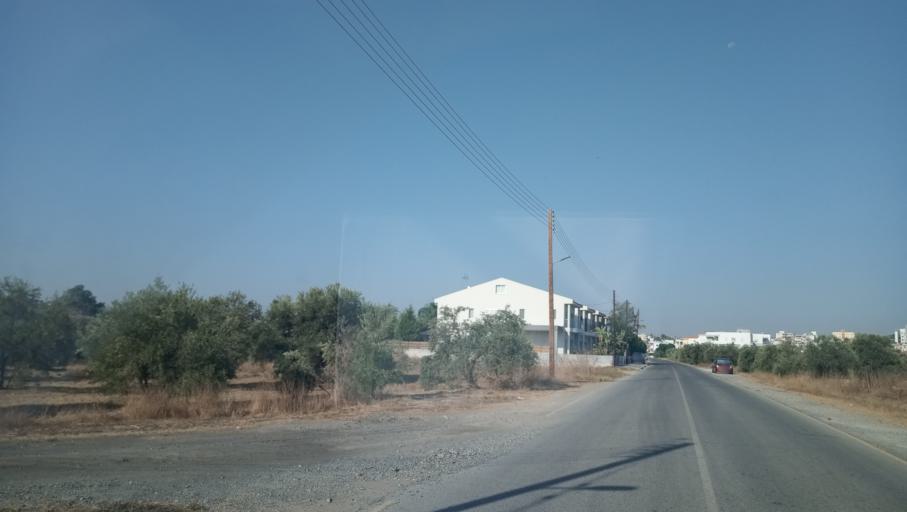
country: CY
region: Lefkosia
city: Geri
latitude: 35.1086
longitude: 33.4317
